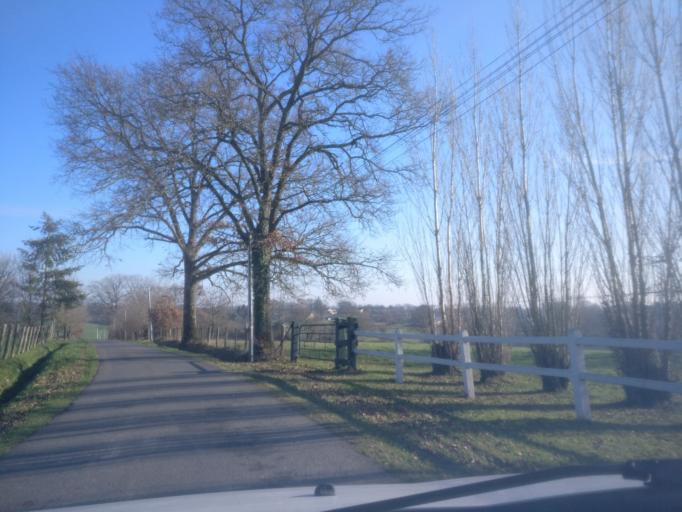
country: FR
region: Brittany
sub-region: Departement d'Ille-et-Vilaine
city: Livre-sur-Changeon
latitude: 48.2408
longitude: -1.3478
